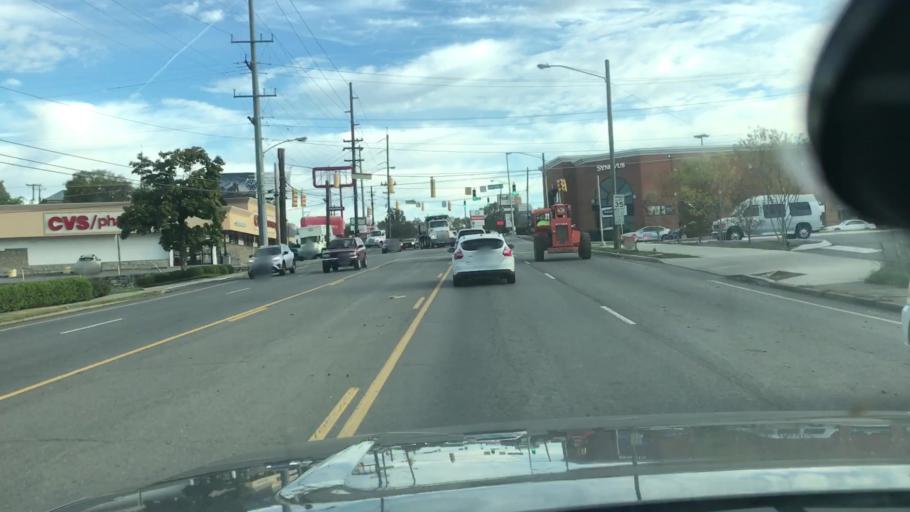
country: US
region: Tennessee
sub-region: Davidson County
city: Oak Hill
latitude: 36.1082
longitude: -86.8124
